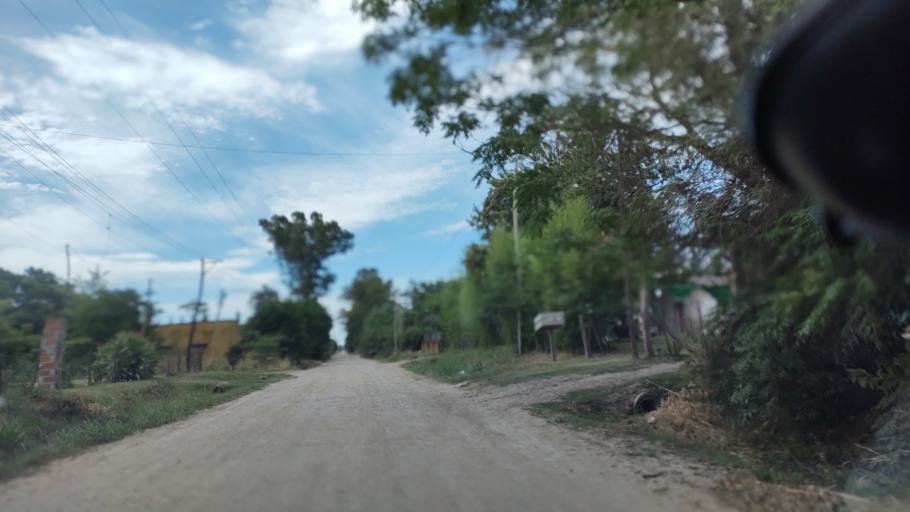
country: AR
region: Buenos Aires
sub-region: Partido de Lobos
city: Lobos
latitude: -35.1734
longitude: -59.1086
